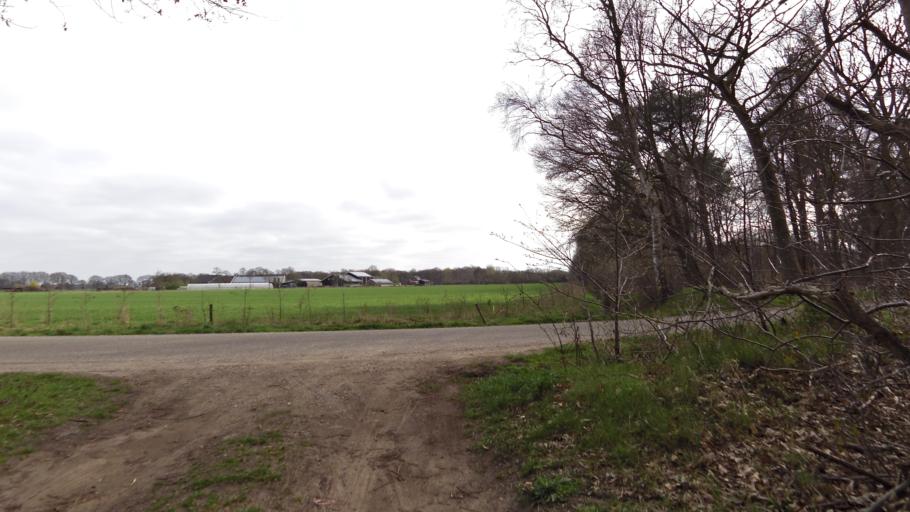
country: NL
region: Gelderland
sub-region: Gemeente Barneveld
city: Voorthuizen
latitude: 52.2003
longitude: 5.5836
